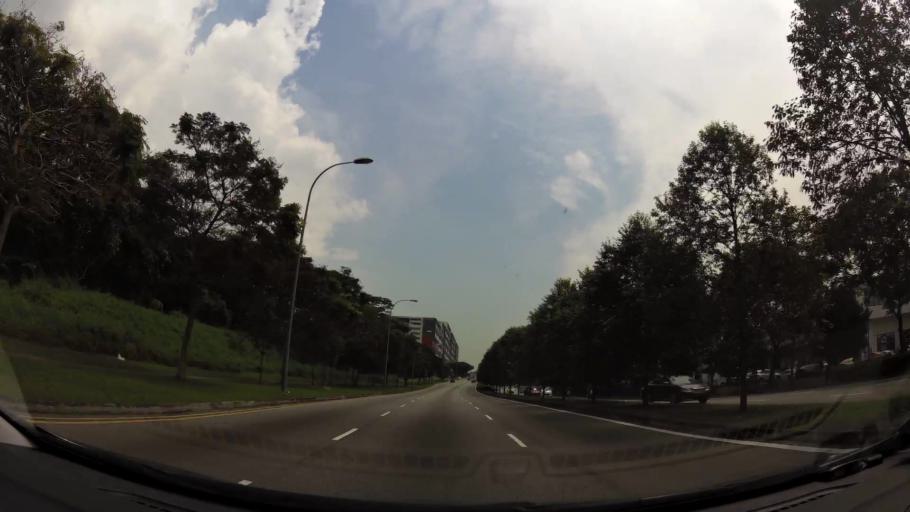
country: SG
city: Singapore
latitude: 1.3387
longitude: 103.9022
